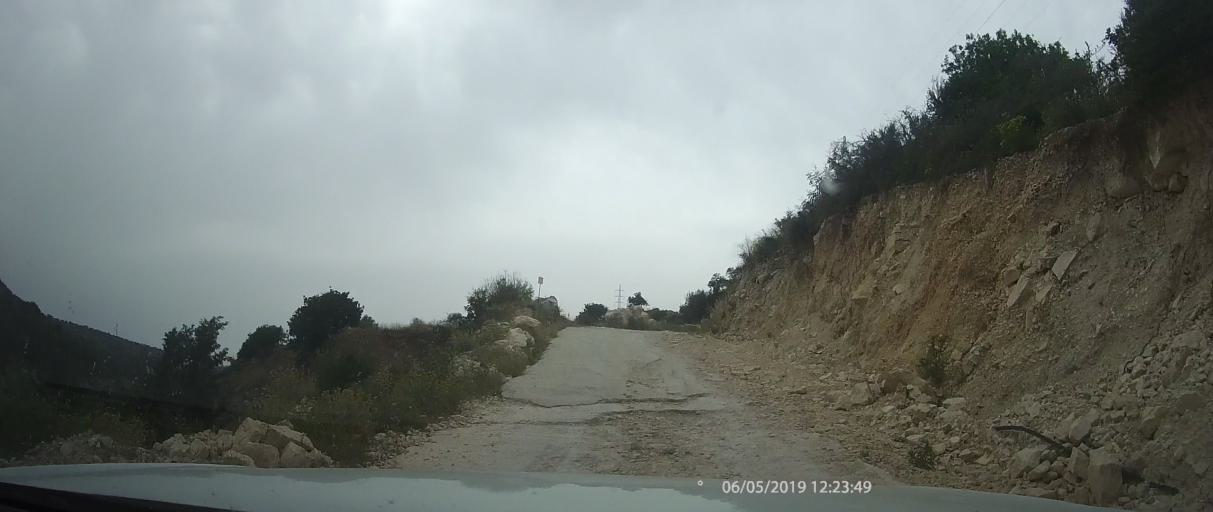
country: CY
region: Pafos
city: Tala
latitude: 34.8686
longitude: 32.4342
